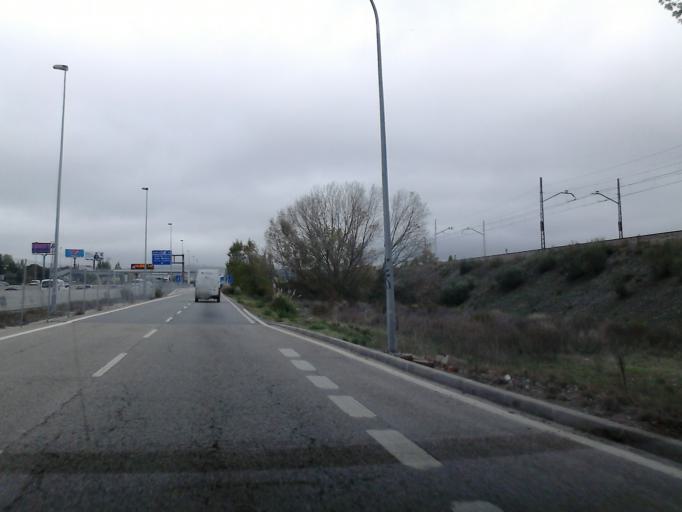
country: ES
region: Madrid
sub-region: Provincia de Madrid
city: Las Matas
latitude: 40.5388
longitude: -3.8905
